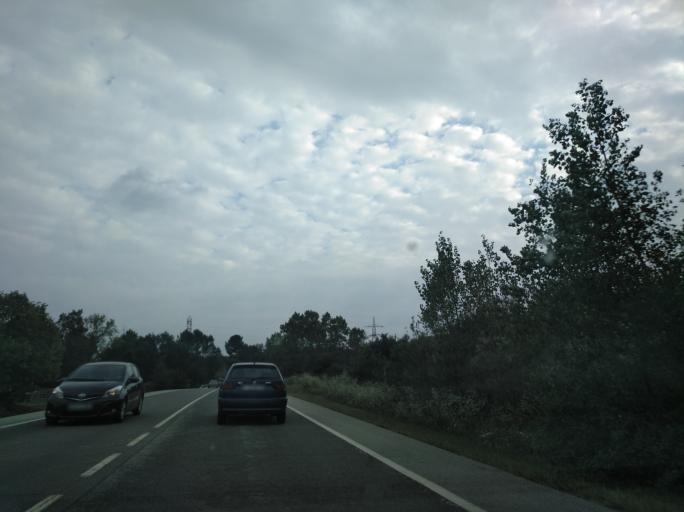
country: ES
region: Catalonia
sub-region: Provincia de Girona
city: Angles
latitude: 41.9283
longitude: 2.6502
